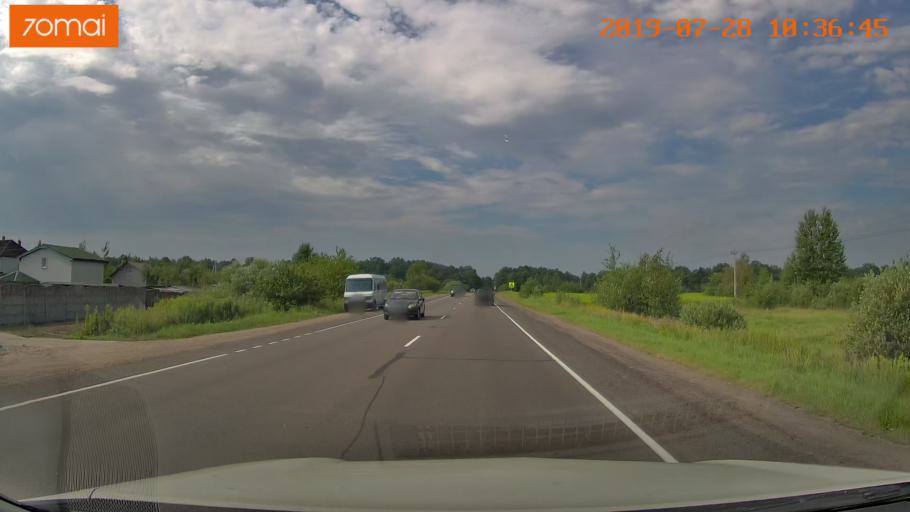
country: RU
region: Kaliningrad
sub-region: Gorod Kaliningrad
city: Kaliningrad
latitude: 54.7360
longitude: 20.4179
